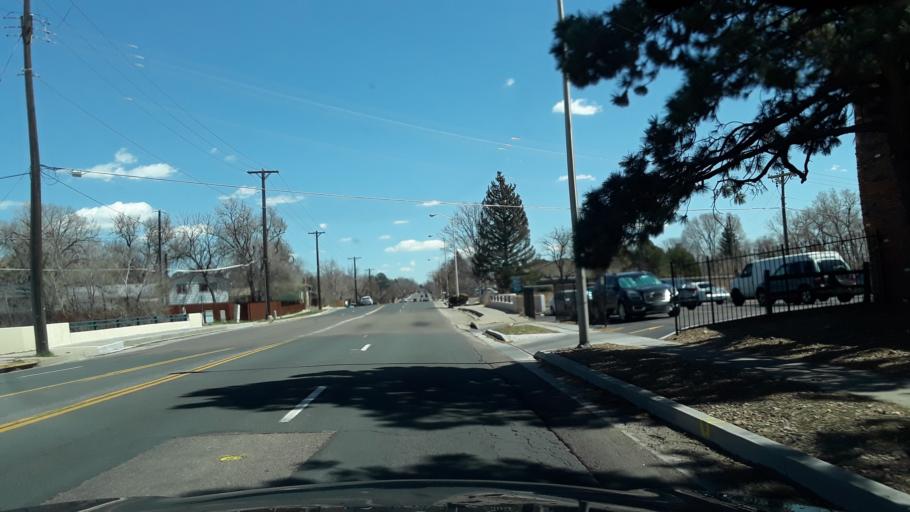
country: US
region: Colorado
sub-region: El Paso County
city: Cimarron Hills
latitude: 38.8543
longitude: -104.7524
